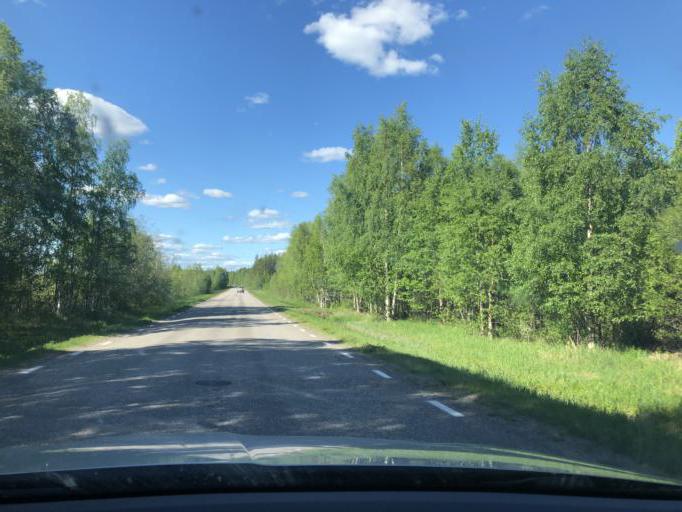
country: SE
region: Norrbotten
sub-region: Kalix Kommun
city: Kalix
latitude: 65.9132
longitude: 23.1734
